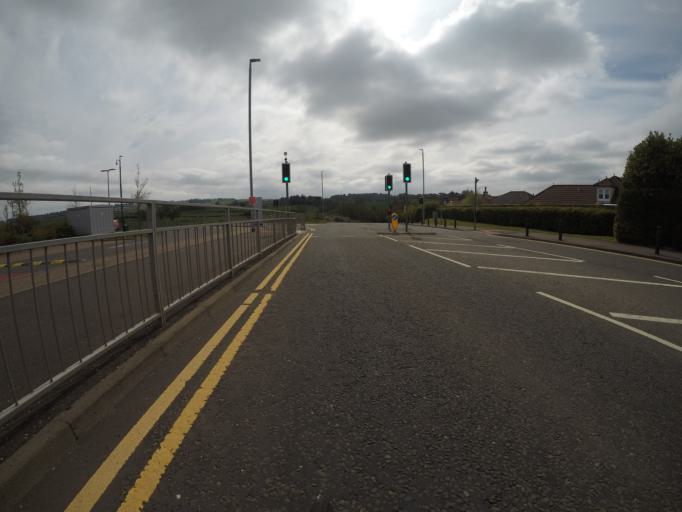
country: GB
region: Scotland
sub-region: East Renfrewshire
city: Newton Mearns
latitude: 55.7677
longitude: -4.3082
